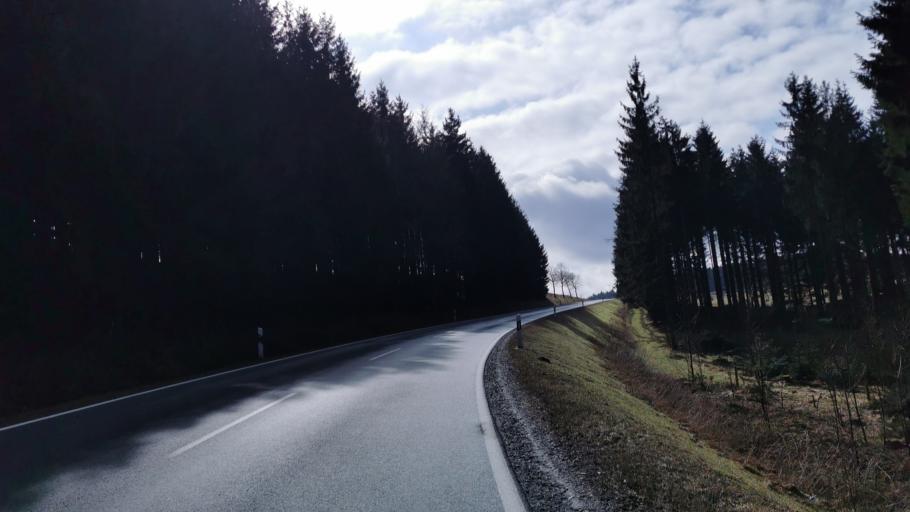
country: DE
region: Bavaria
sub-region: Upper Franconia
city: Reichenbach
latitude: 50.4248
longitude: 11.4036
